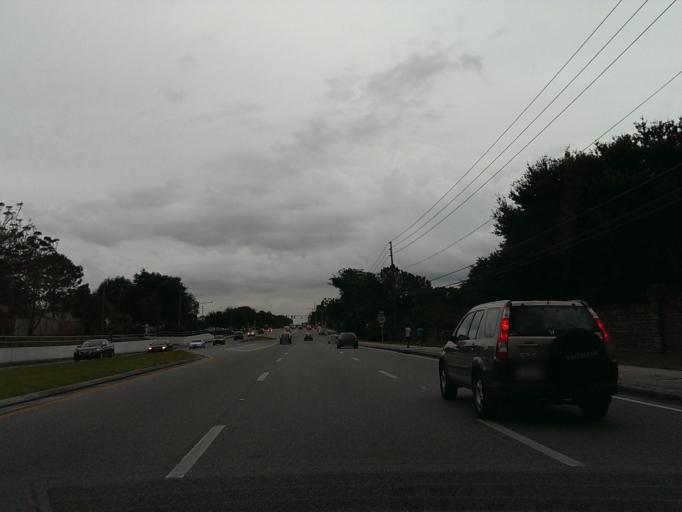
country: US
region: Florida
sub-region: Orange County
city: Orlovista
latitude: 28.5395
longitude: -81.4793
